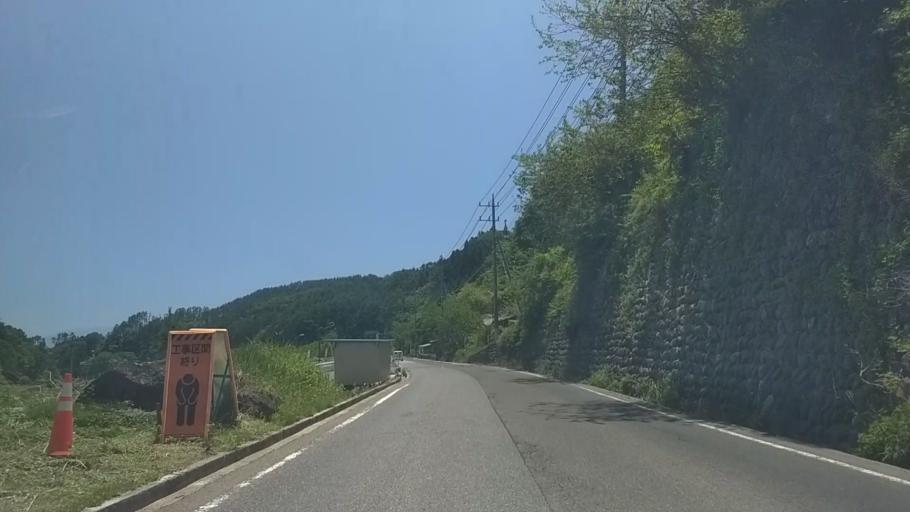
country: JP
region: Yamanashi
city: Nirasaki
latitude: 35.8700
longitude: 138.4275
